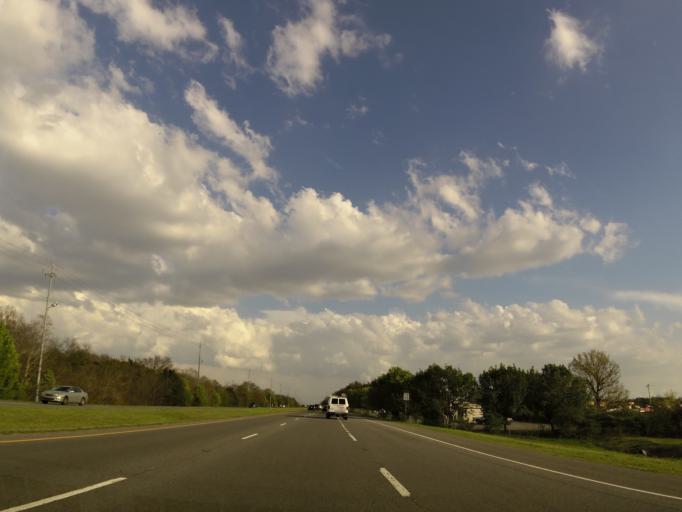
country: US
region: Tennessee
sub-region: Rutherford County
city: Murfreesboro
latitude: 35.8970
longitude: -86.4442
